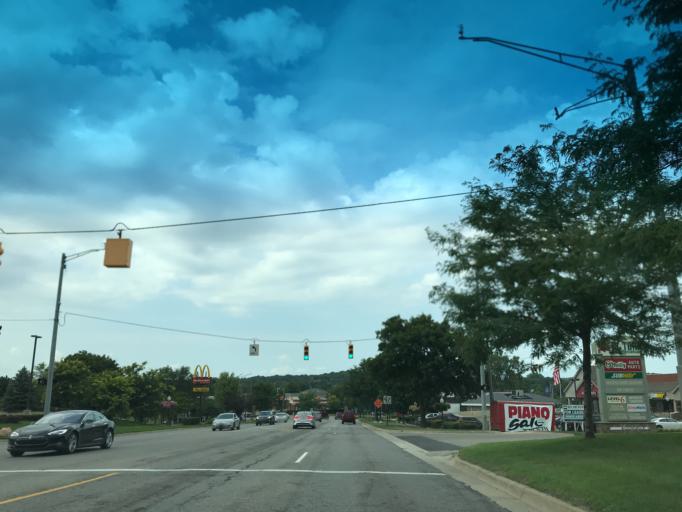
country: US
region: Michigan
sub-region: Oakland County
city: Milford
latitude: 42.5810
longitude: -83.6109
